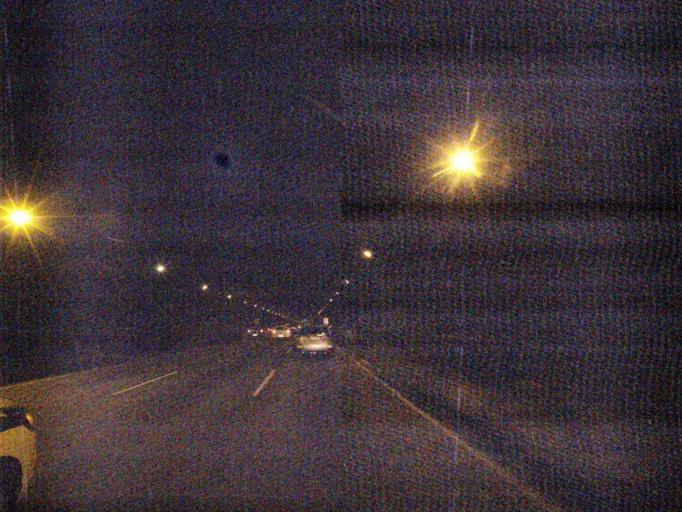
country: BR
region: Rio de Janeiro
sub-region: Rio De Janeiro
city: Rio de Janeiro
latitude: -22.9518
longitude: -43.2048
